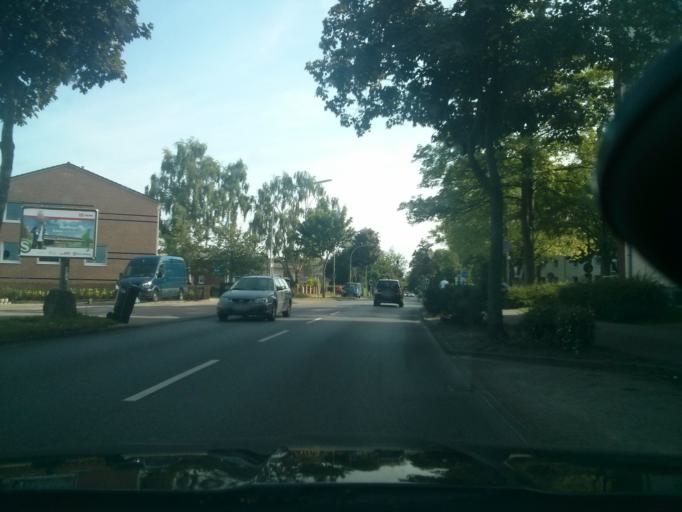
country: DE
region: Schleswig-Holstein
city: Halstenbek
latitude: 53.5986
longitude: 9.8381
